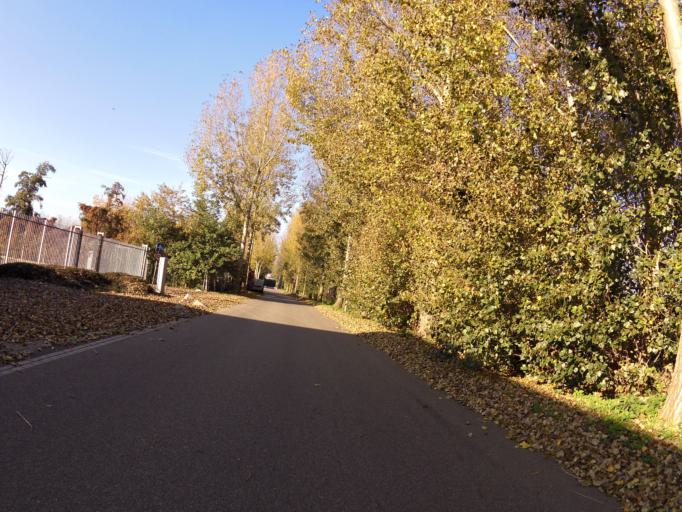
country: NL
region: North Brabant
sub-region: Gemeente 's-Hertogenbosch
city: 's-Hertogenbosch
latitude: 51.7063
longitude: 5.2976
